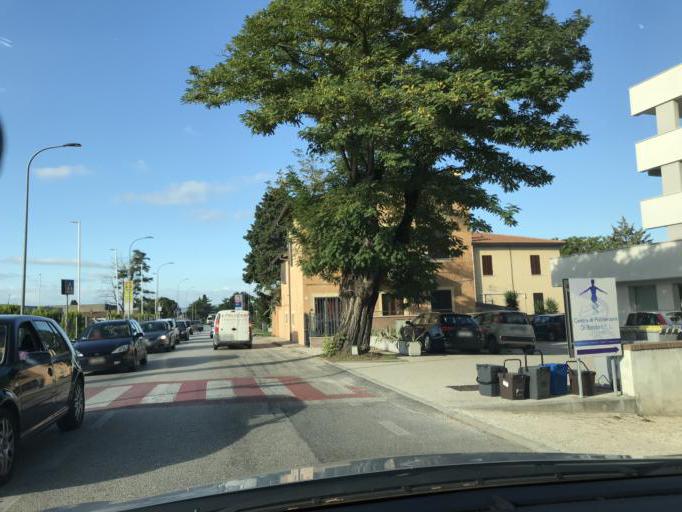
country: IT
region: Umbria
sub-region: Provincia di Perugia
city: Foligno
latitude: 42.9643
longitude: 12.6885
